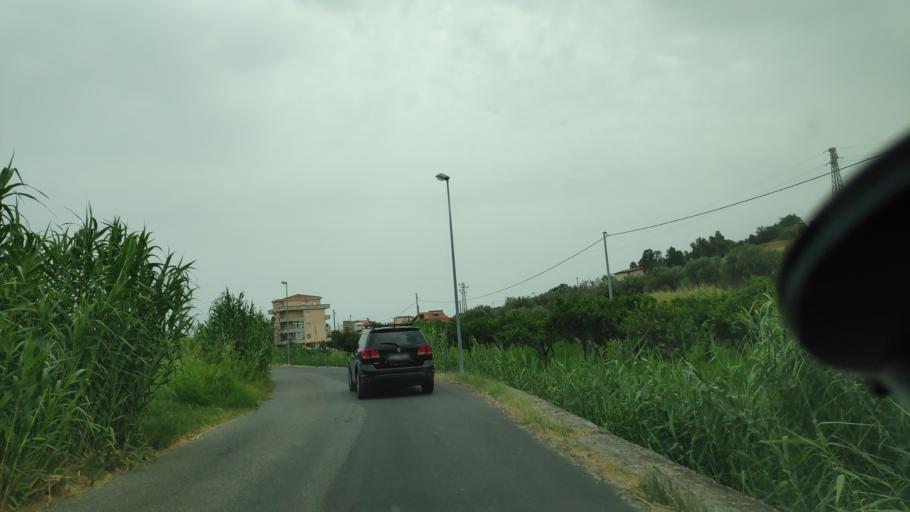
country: IT
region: Calabria
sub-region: Provincia di Catanzaro
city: Marina di Davoli
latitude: 38.6618
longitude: 16.5411
